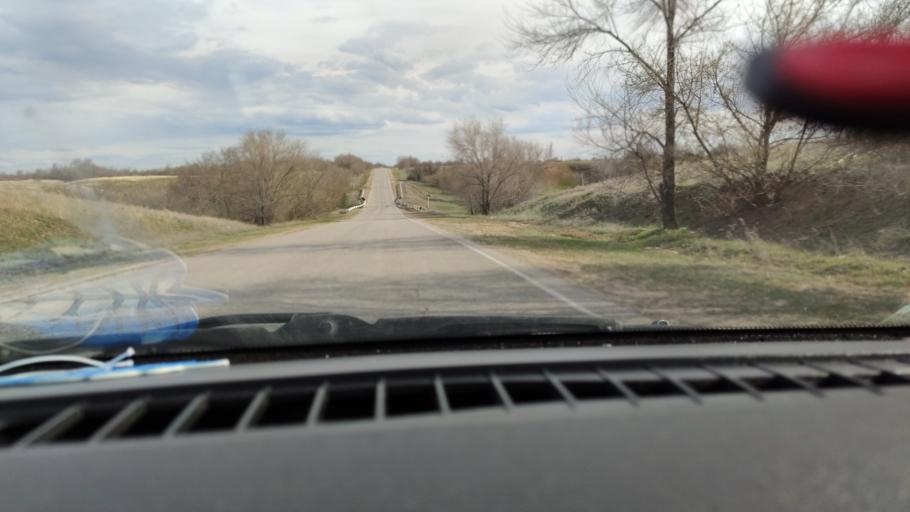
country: RU
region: Saratov
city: Rovnoye
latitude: 50.9870
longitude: 46.1121
